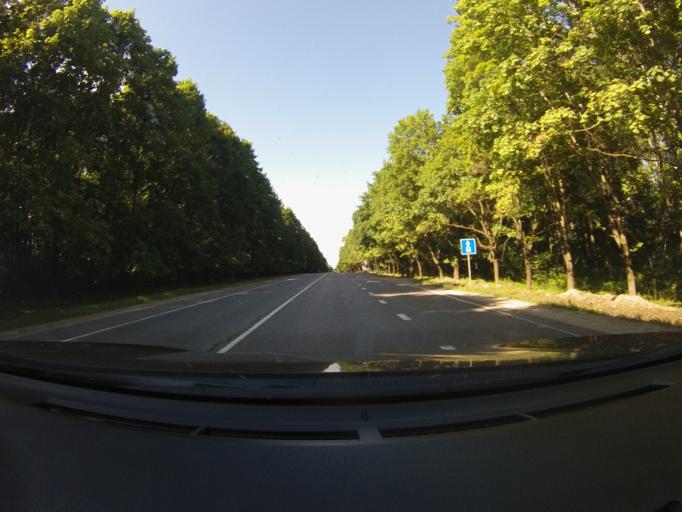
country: RU
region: Orjol
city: Spasskoye-Lutovinovo
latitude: 53.3790
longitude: 36.7398
